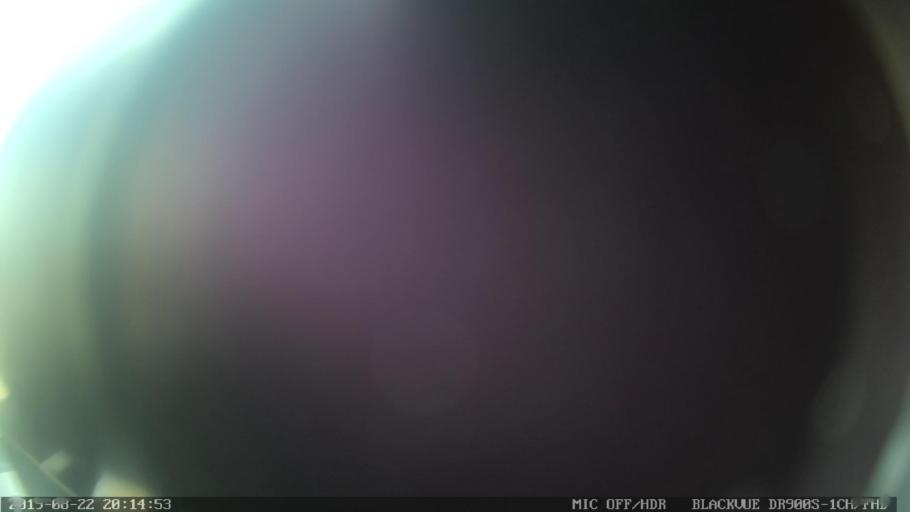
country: PT
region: Guarda
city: Alcains
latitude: 39.9212
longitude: -7.4340
